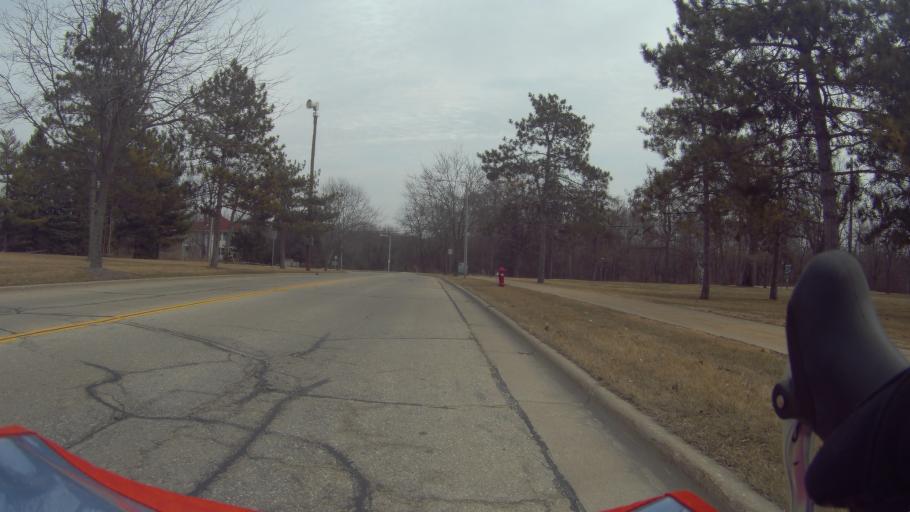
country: US
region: Wisconsin
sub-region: Dane County
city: Maple Bluff
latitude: 43.1343
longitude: -89.3963
